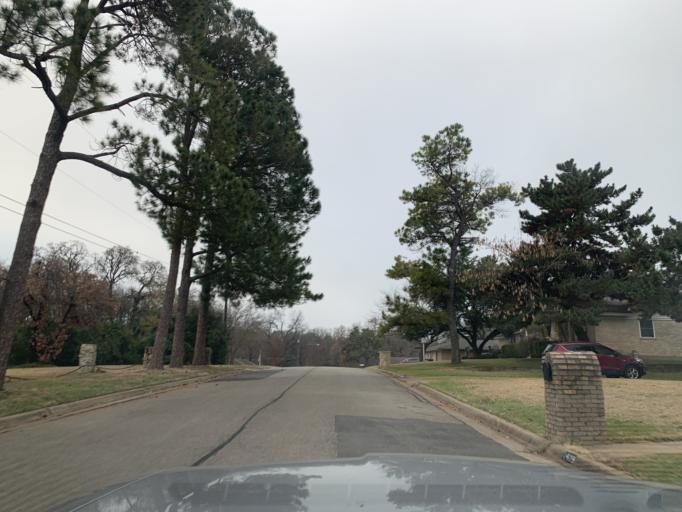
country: US
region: Texas
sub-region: Tarrant County
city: Bedford
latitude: 32.8333
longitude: -97.1523
